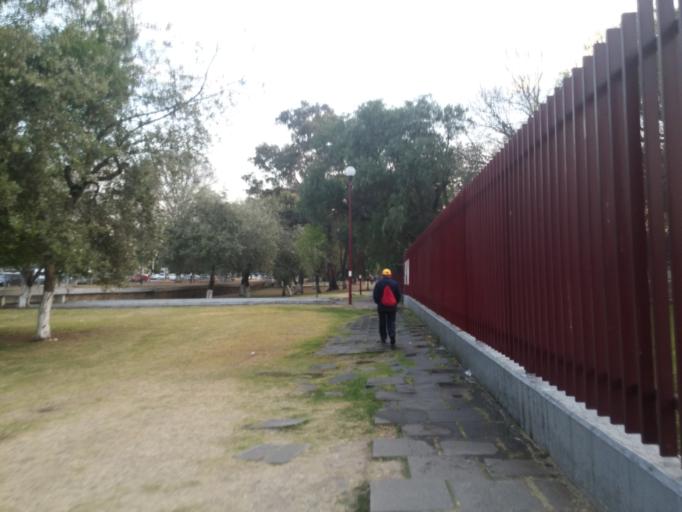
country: MX
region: Mexico
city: Colonia Lindavista
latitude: 19.5021
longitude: -99.1361
